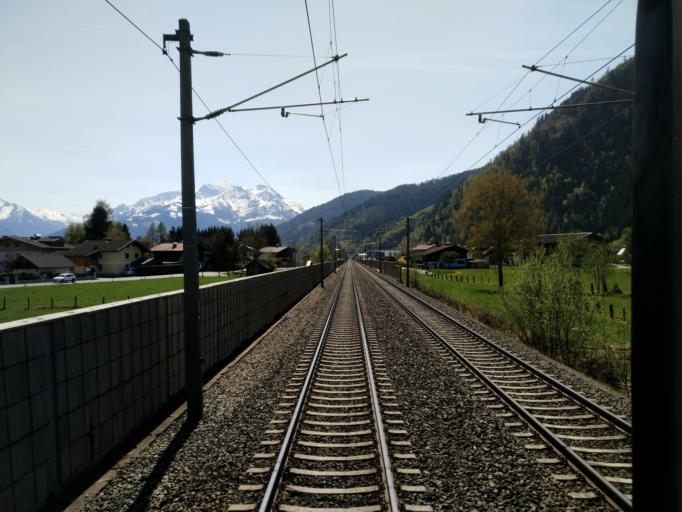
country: AT
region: Salzburg
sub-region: Politischer Bezirk Zell am See
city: Maishofen
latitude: 47.3521
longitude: 12.8062
